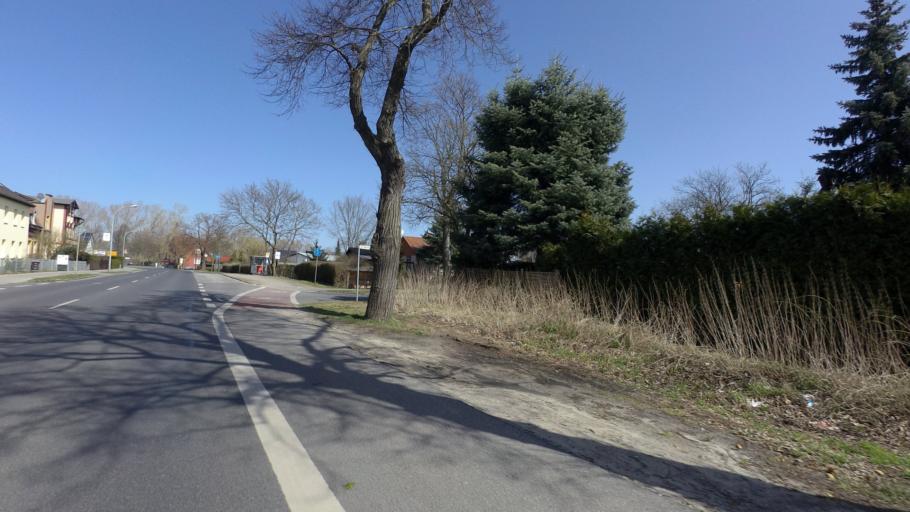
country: DE
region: Brandenburg
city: Oranienburg
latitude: 52.7716
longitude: 13.2471
